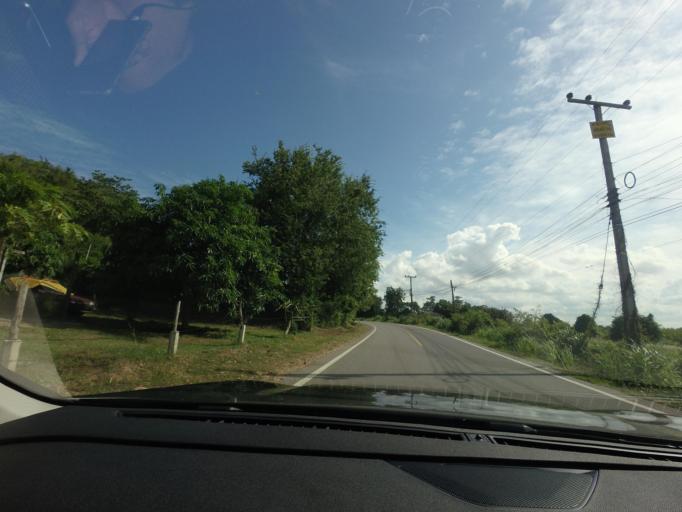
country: TH
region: Prachuap Khiri Khan
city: Pran Buri
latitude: 12.4563
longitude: 99.9438
